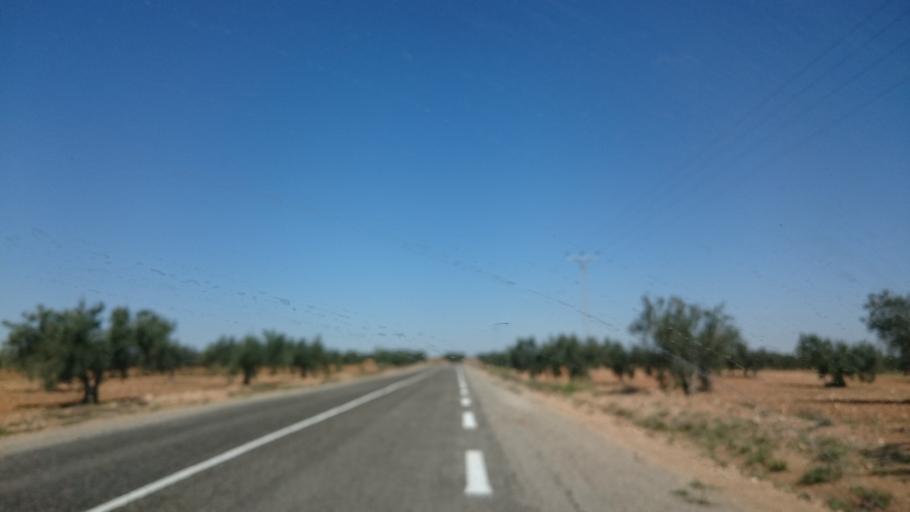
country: TN
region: Safaqis
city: Bi'r `Ali Bin Khalifah
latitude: 34.8992
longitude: 10.3921
